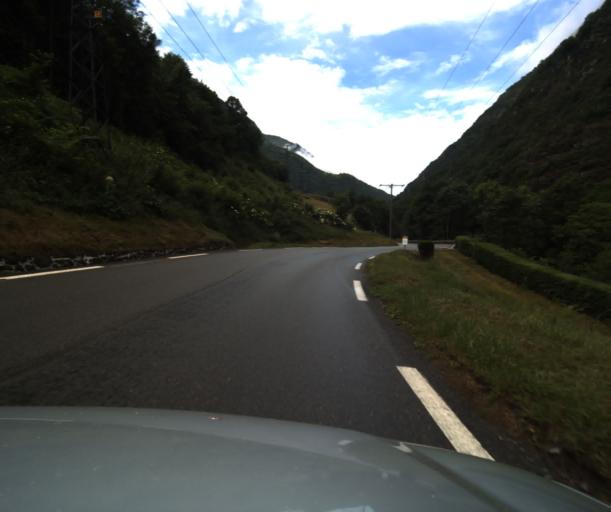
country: FR
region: Midi-Pyrenees
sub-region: Departement des Hautes-Pyrenees
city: Luz-Saint-Sauveur
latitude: 42.8332
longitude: 0.0002
